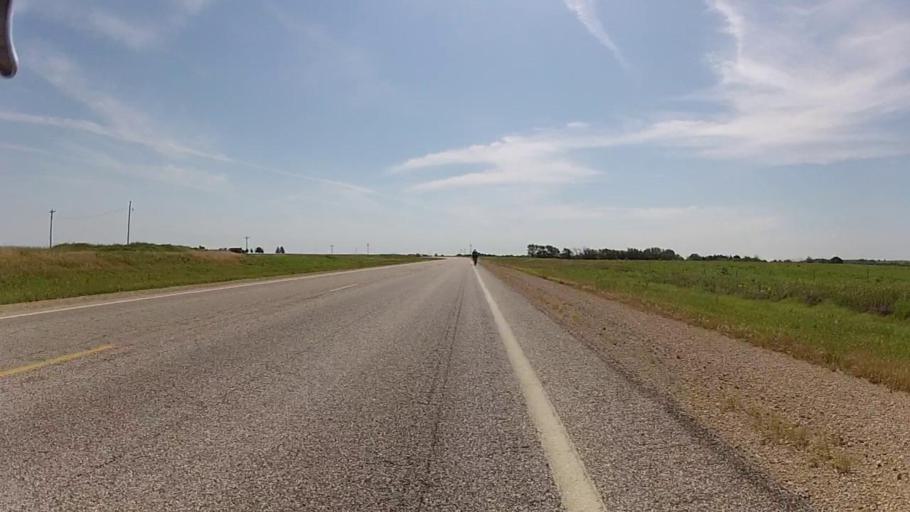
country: US
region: Kansas
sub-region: Chautauqua County
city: Sedan
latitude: 37.1101
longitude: -96.5200
